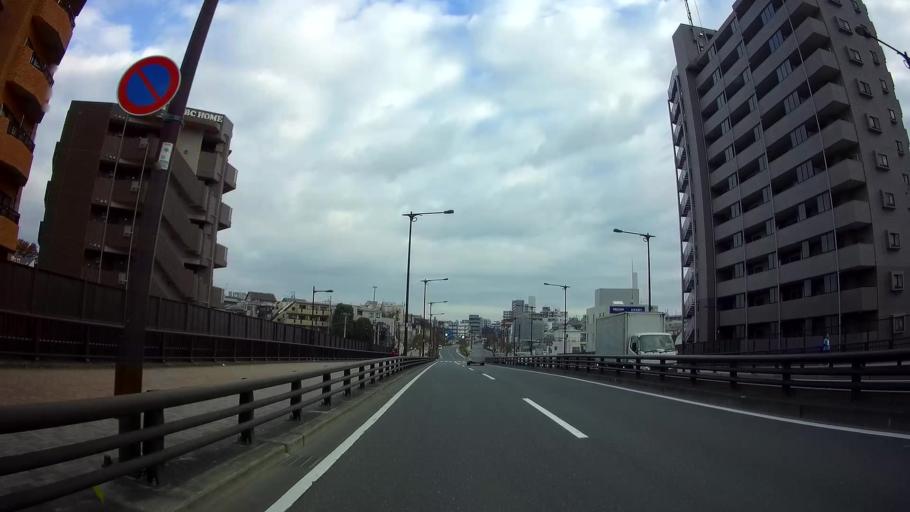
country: JP
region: Tokyo
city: Tokyo
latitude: 35.7150
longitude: 139.6868
